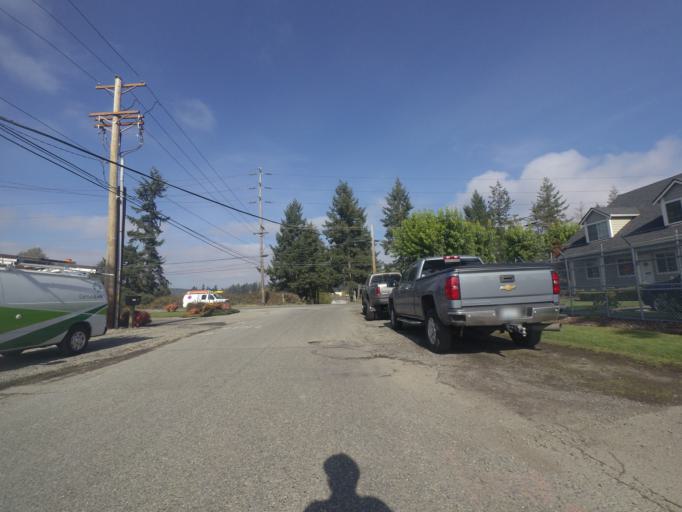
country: US
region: Washington
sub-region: Pierce County
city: Lakewood
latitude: 47.1890
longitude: -122.5163
